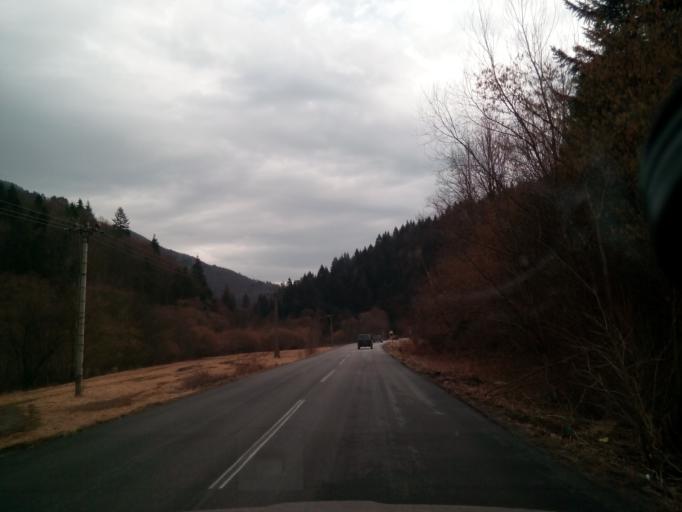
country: SK
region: Zilinsky
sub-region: Okres Zilina
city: Terchova
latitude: 49.2319
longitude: 19.1539
